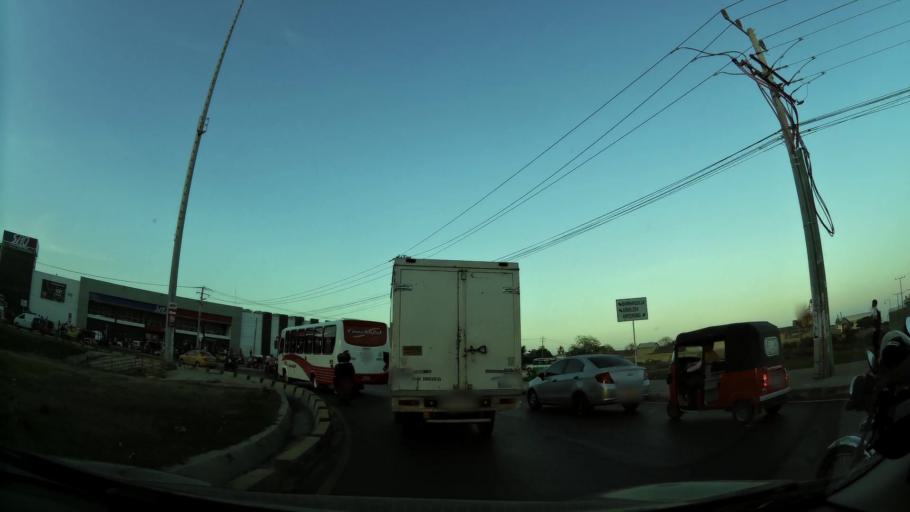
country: CO
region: Atlantico
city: Soledad
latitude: 10.9267
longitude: -74.7783
